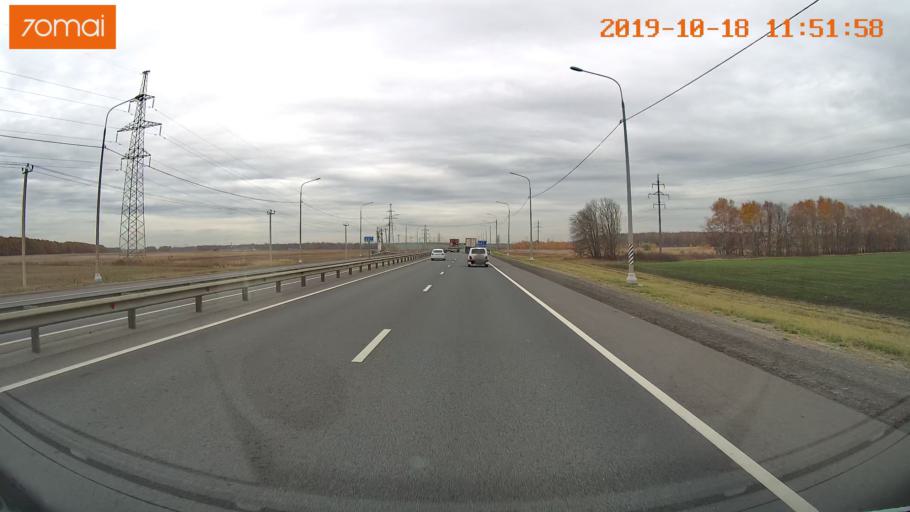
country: RU
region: Rjazan
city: Mikhaylov
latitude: 54.2519
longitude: 39.0371
